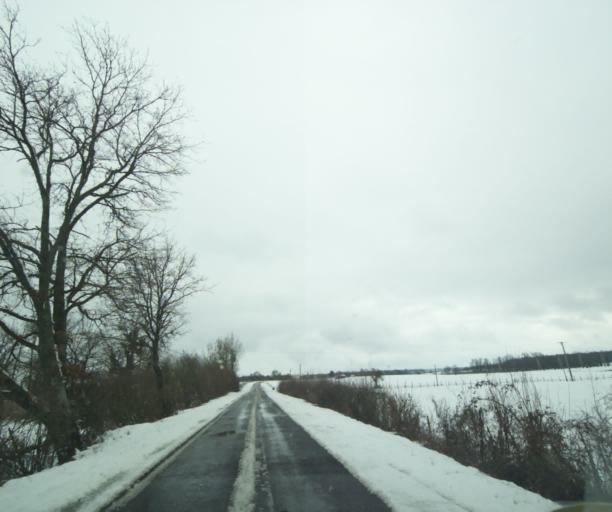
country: FR
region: Champagne-Ardenne
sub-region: Departement de la Haute-Marne
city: Montier-en-Der
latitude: 48.4197
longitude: 4.7309
